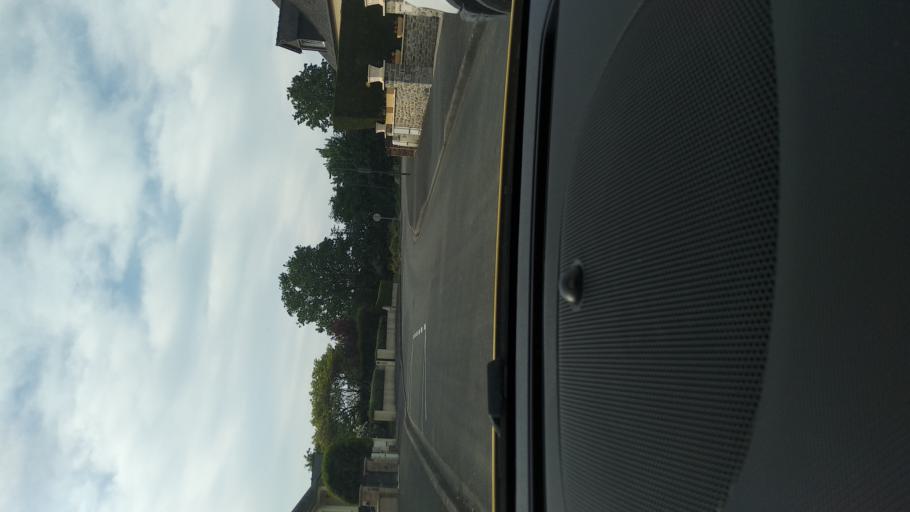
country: FR
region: Pays de la Loire
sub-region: Departement de la Mayenne
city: Change
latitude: 48.0981
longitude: -0.7982
